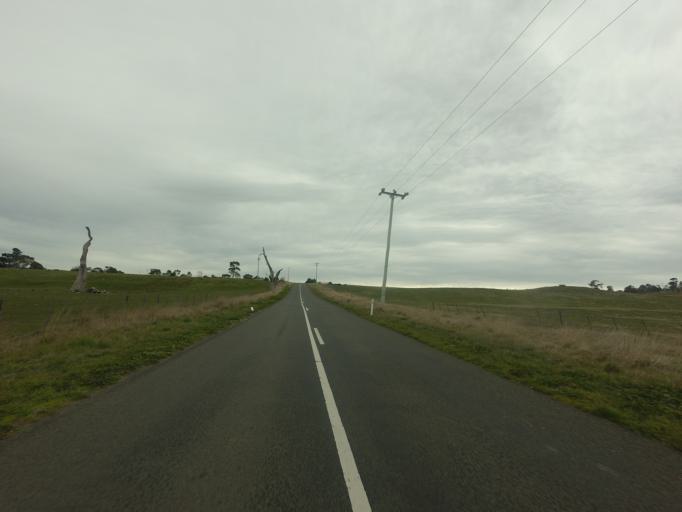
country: AU
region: Tasmania
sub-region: Derwent Valley
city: New Norfolk
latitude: -42.4061
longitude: 147.0083
